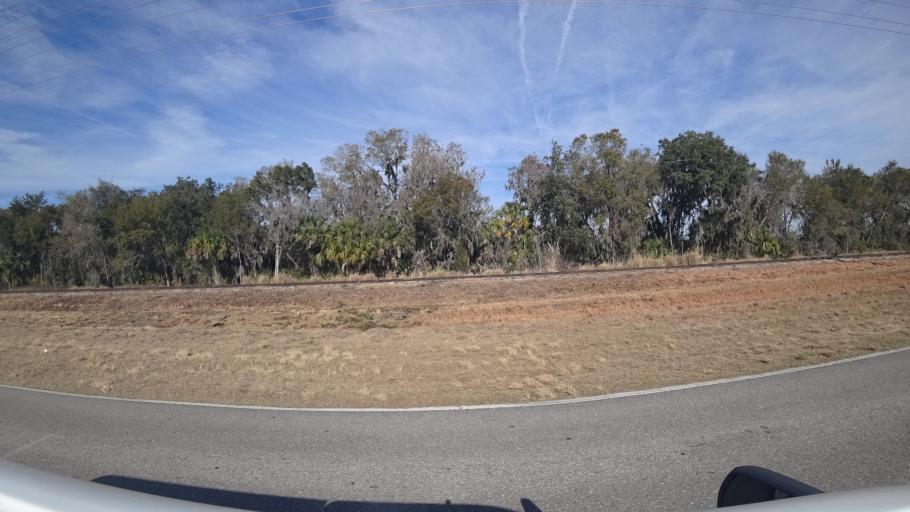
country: US
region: Florida
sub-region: Manatee County
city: Ellenton
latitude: 27.5731
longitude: -82.4741
